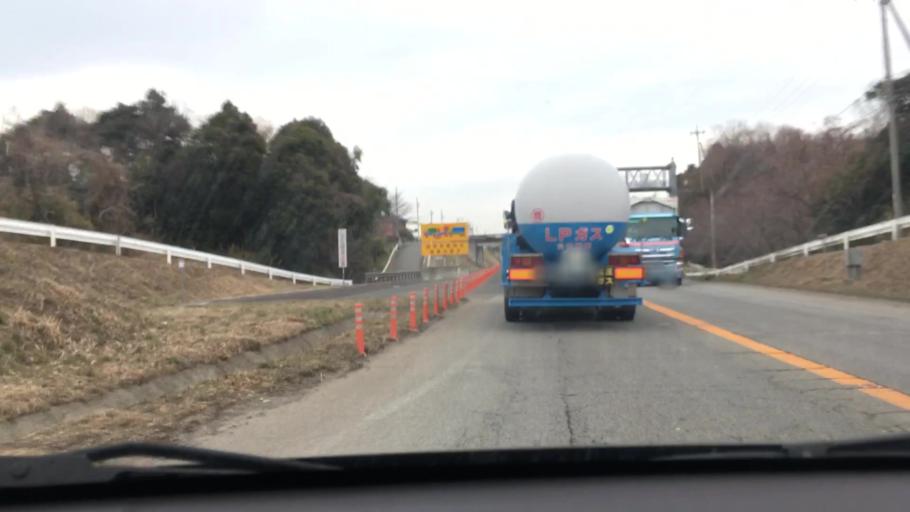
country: JP
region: Mie
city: Kameyama
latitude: 34.8643
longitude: 136.4482
